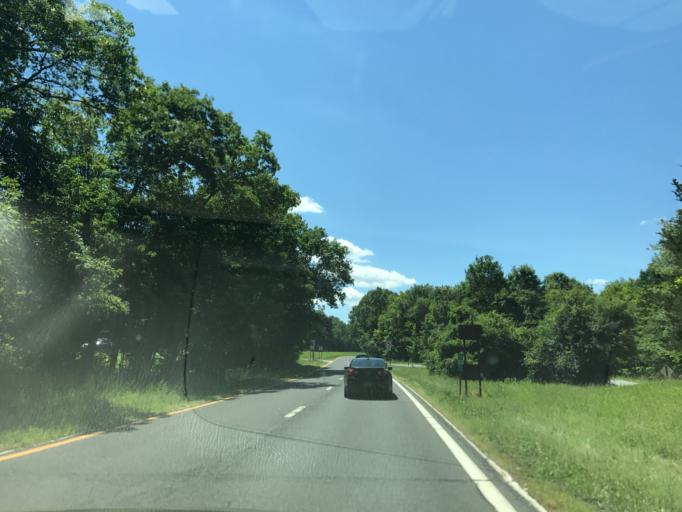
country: US
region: New York
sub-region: Dutchess County
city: Pleasant Valley
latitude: 41.7155
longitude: -73.7839
